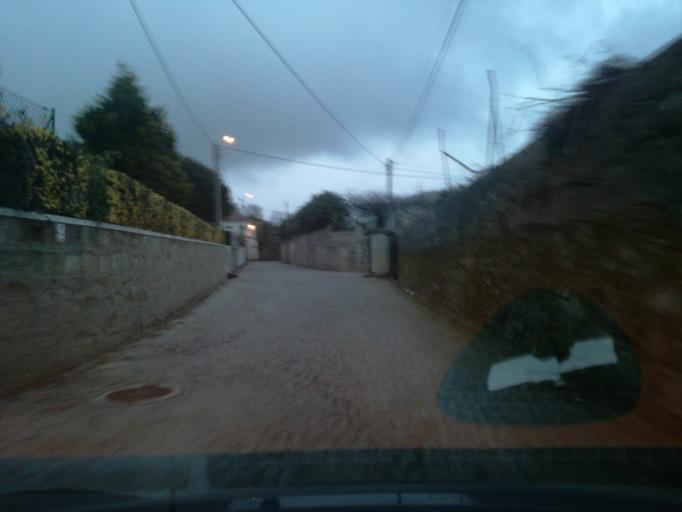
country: PT
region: Porto
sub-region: Maia
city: Gemunde
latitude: 41.2683
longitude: -8.6633
